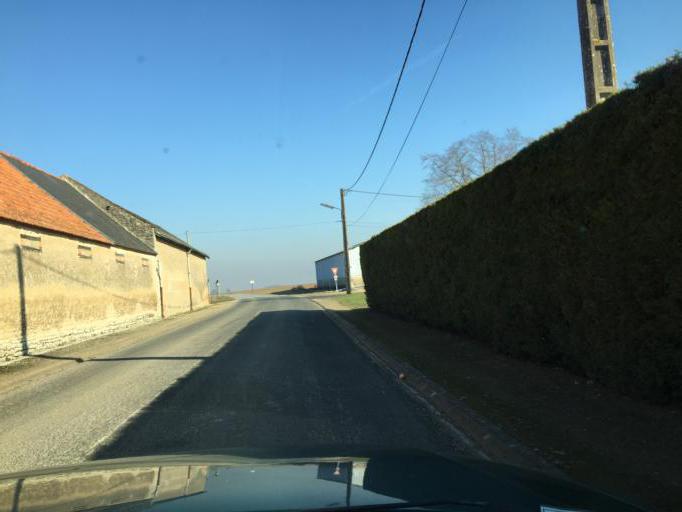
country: FR
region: Centre
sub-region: Departement du Loiret
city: Patay
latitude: 48.0605
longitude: 1.7339
